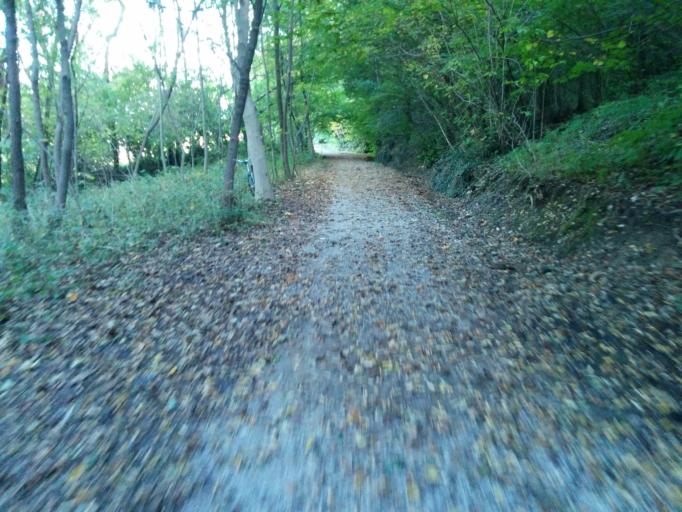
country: IT
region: Friuli Venezia Giulia
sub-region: Provincia di Udine
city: Buia
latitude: 46.2200
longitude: 13.1222
